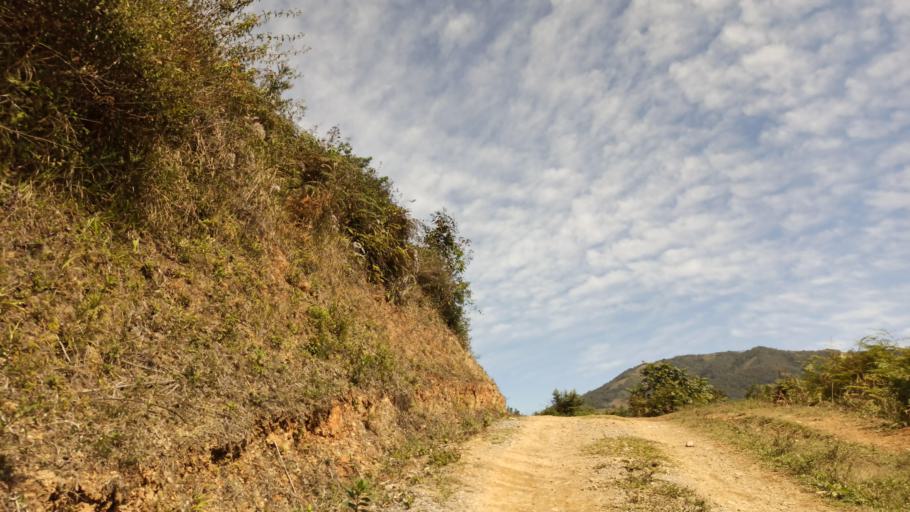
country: MX
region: Veracruz
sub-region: La Perla
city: Metlac Hernandez (Metlac Primero)
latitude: 18.9719
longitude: -97.1011
